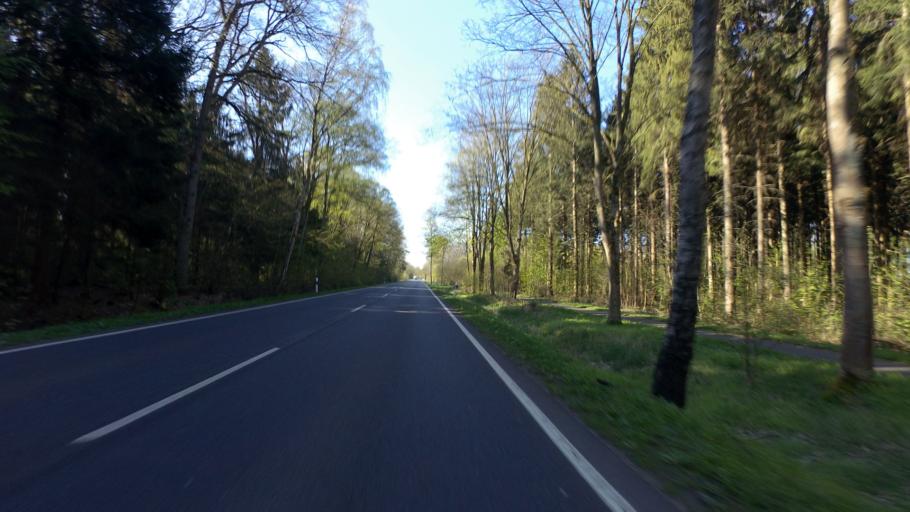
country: DE
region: Lower Saxony
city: Steimbke
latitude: 52.6545
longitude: 9.4478
